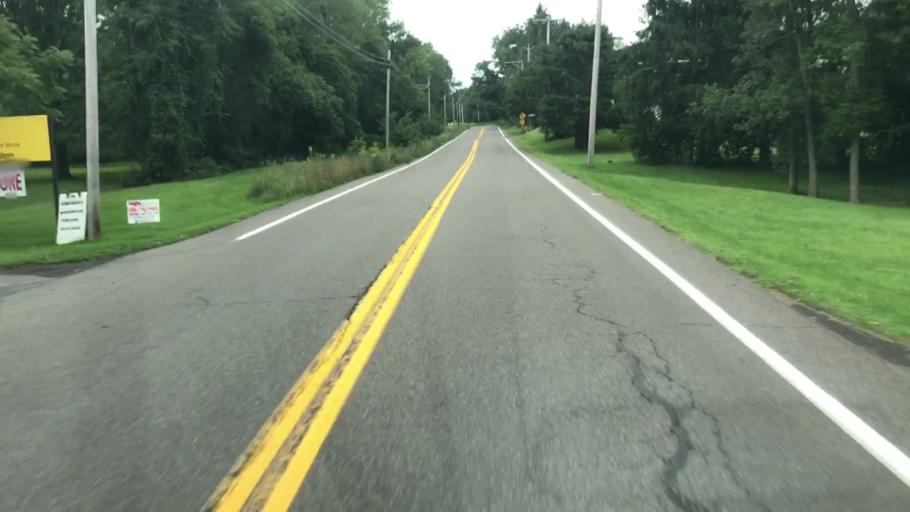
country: US
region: New York
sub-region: Onondaga County
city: Skaneateles
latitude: 42.9830
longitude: -76.4488
